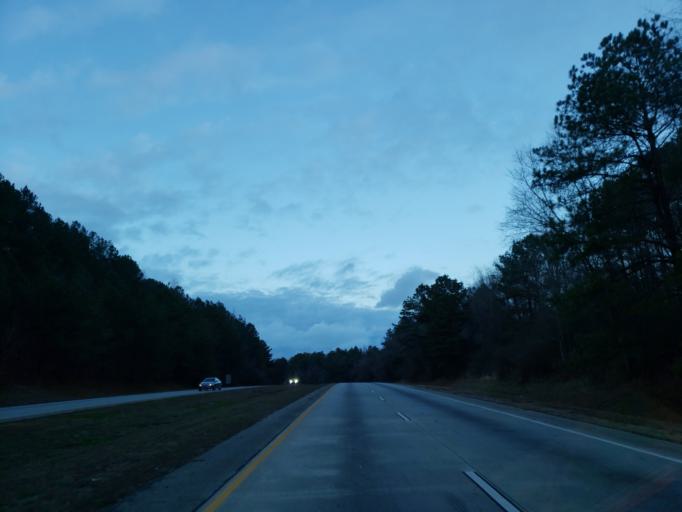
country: US
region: Georgia
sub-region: Fulton County
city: Union City
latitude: 33.6770
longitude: -84.5523
